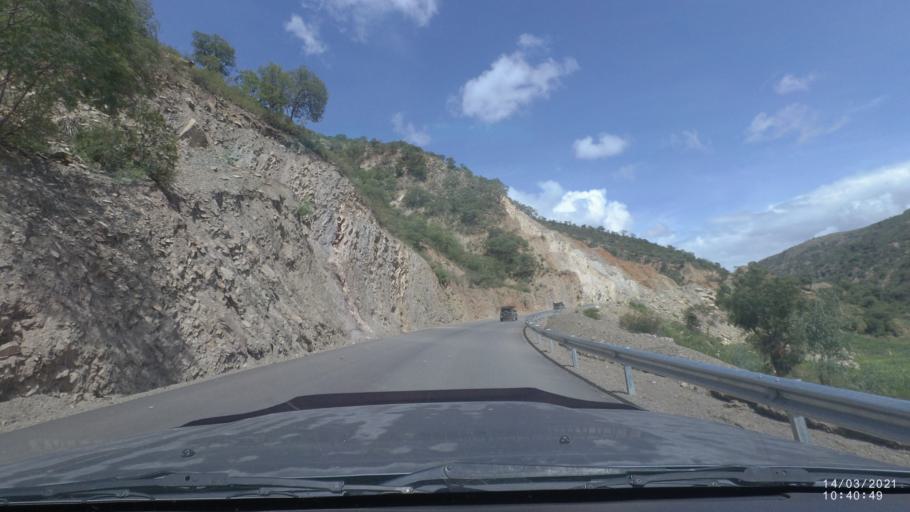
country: BO
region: Cochabamba
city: Cliza
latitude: -17.8817
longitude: -65.9067
